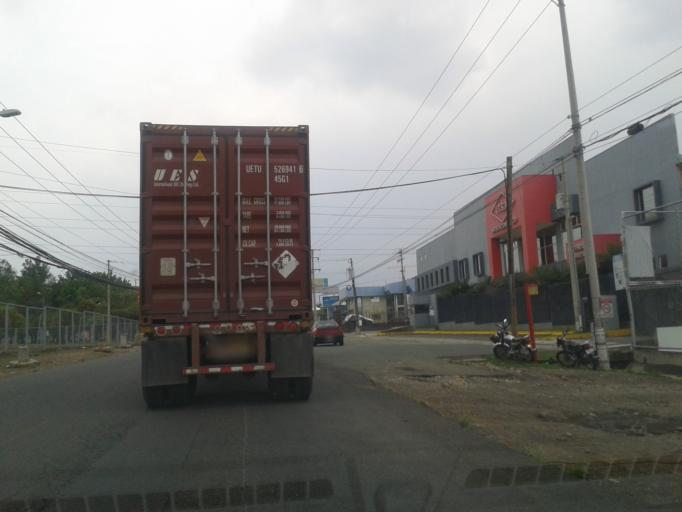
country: CR
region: Heredia
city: San Francisco
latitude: 9.9682
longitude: -84.1248
